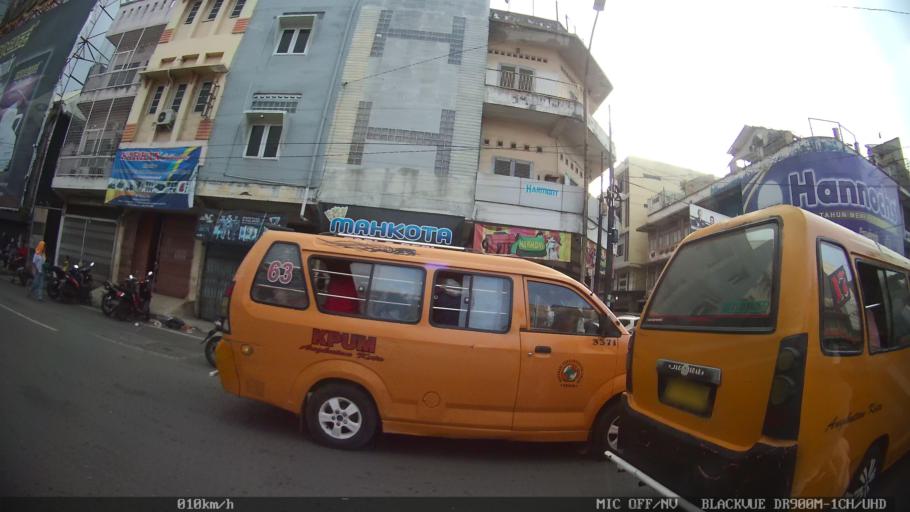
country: ID
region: North Sumatra
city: Medan
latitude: 3.5875
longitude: 98.6856
